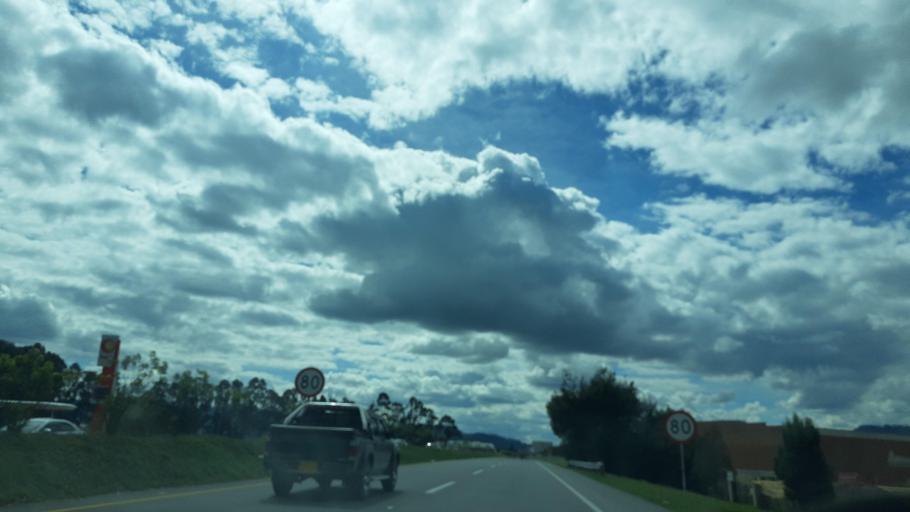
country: CO
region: Cundinamarca
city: Tocancipa
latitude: 4.9555
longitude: -73.9236
